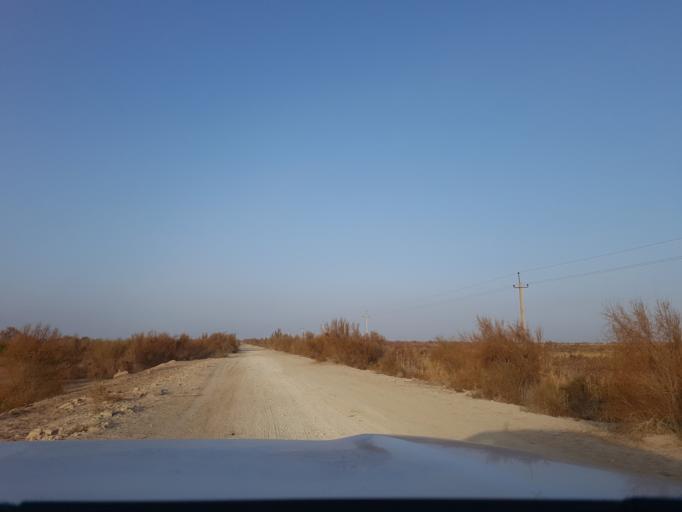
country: TM
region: Dasoguz
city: Koeneuergench
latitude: 41.8522
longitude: 58.2703
